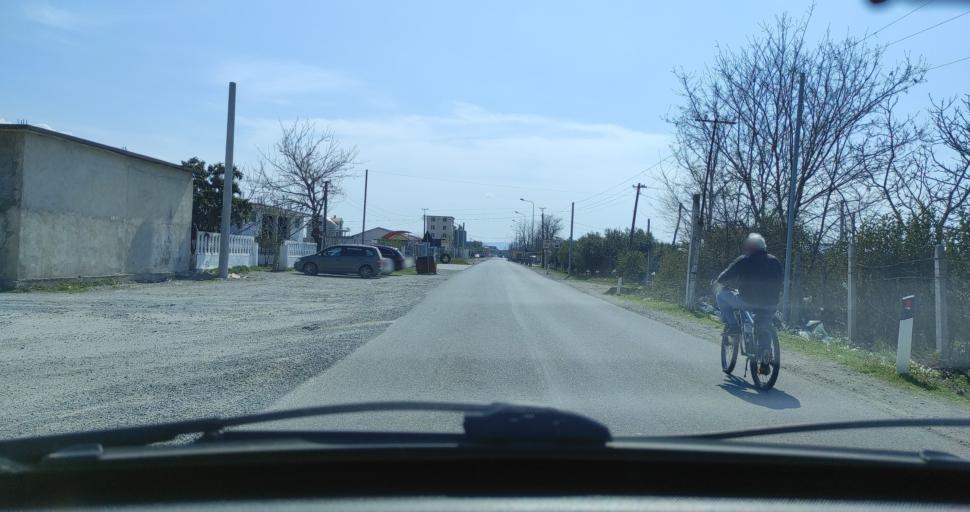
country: AL
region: Shkoder
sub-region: Rrethi i Shkodres
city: Vau i Dejes
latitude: 42.0059
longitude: 19.6182
